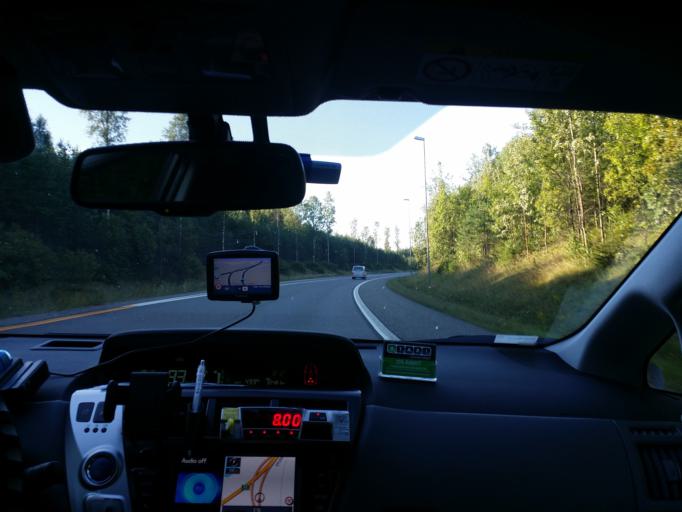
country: NO
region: Akershus
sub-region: Ullensaker
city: Jessheim
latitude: 60.1585
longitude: 11.1488
